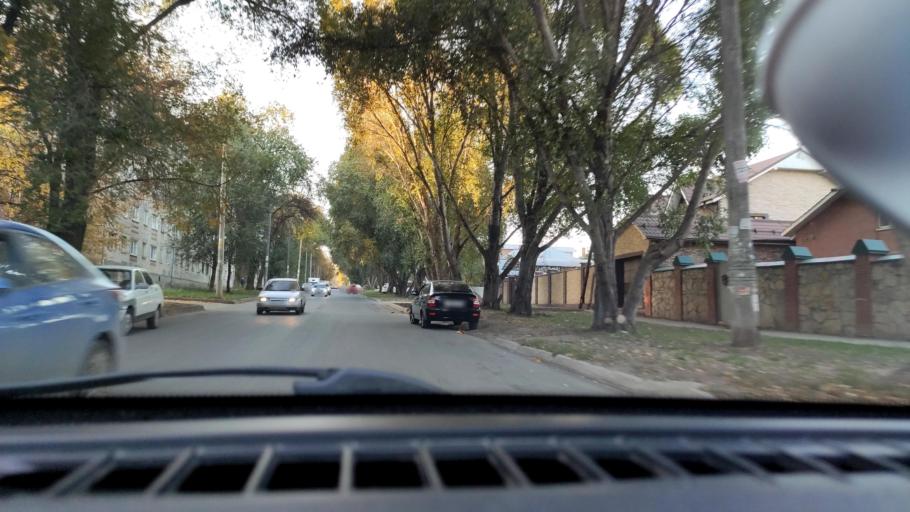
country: RU
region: Samara
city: Samara
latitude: 53.2119
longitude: 50.2349
